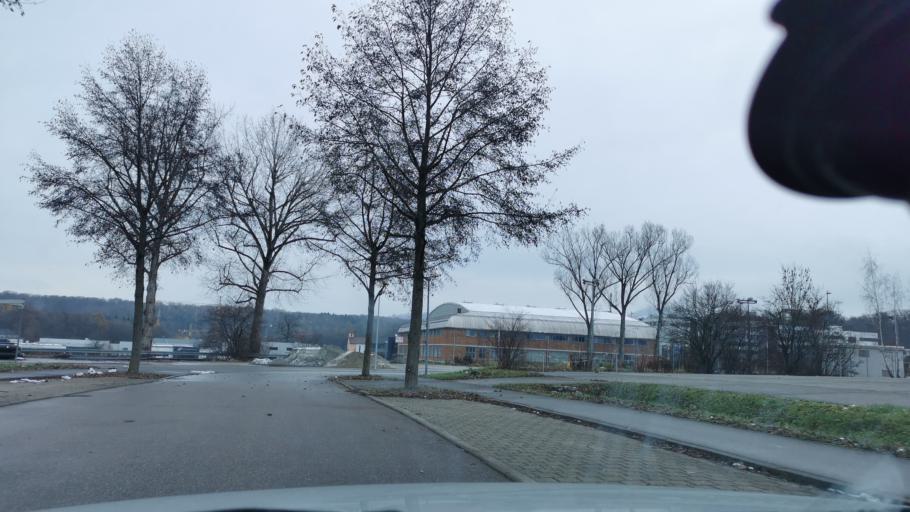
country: DE
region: Baden-Wuerttemberg
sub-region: Regierungsbezirk Stuttgart
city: Eislingen
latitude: 48.7111
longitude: 9.6888
